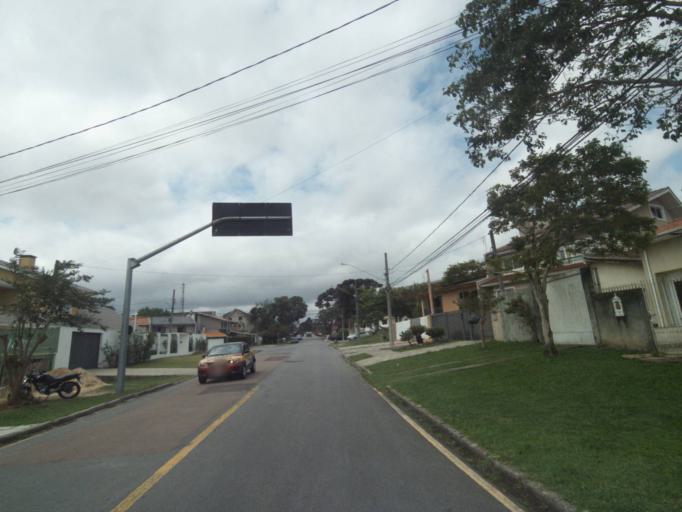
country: BR
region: Parana
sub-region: Pinhais
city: Pinhais
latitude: -25.4356
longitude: -49.2294
